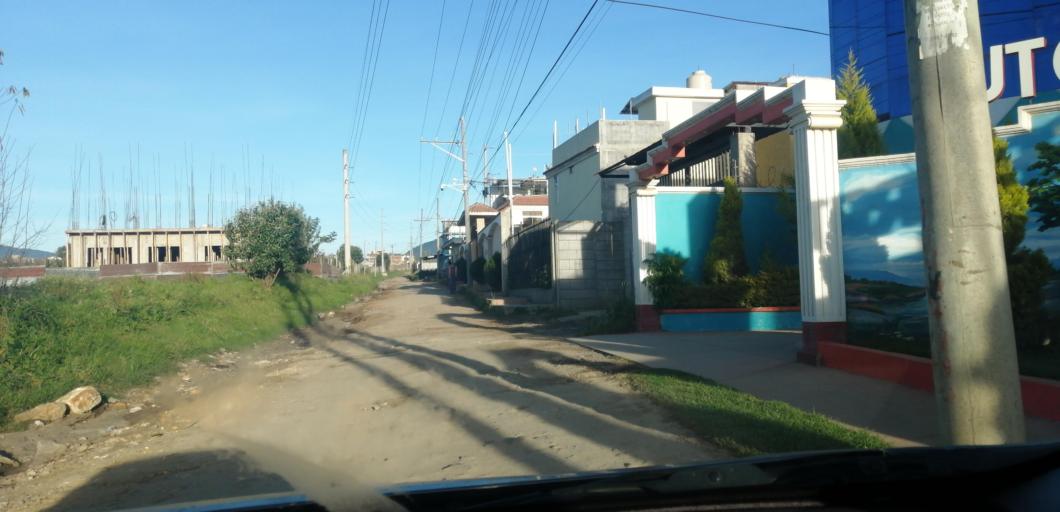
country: GT
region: Quetzaltenango
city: Olintepeque
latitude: 14.8681
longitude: -91.5301
